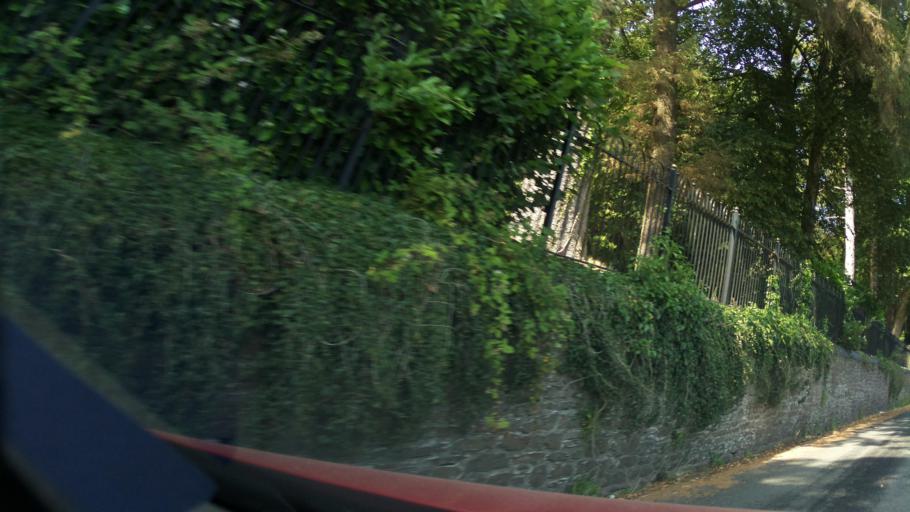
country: GB
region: Wales
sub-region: Caerphilly County Borough
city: Bargoed
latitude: 51.7012
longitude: -3.2293
